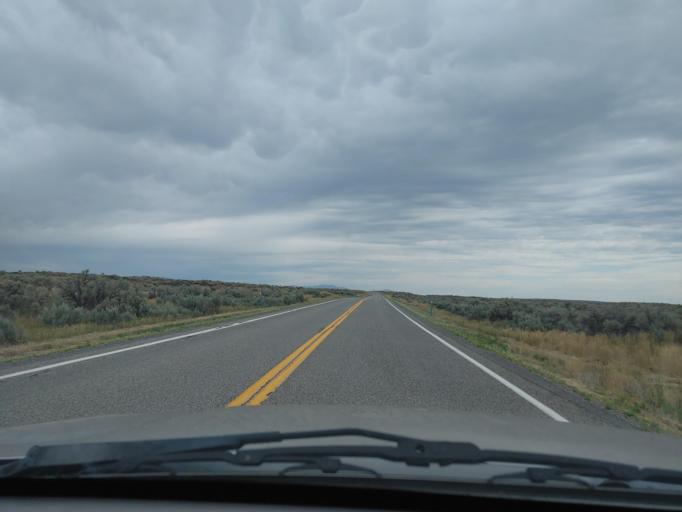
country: US
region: Idaho
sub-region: Lincoln County
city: Shoshone
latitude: 43.0919
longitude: -114.0900
